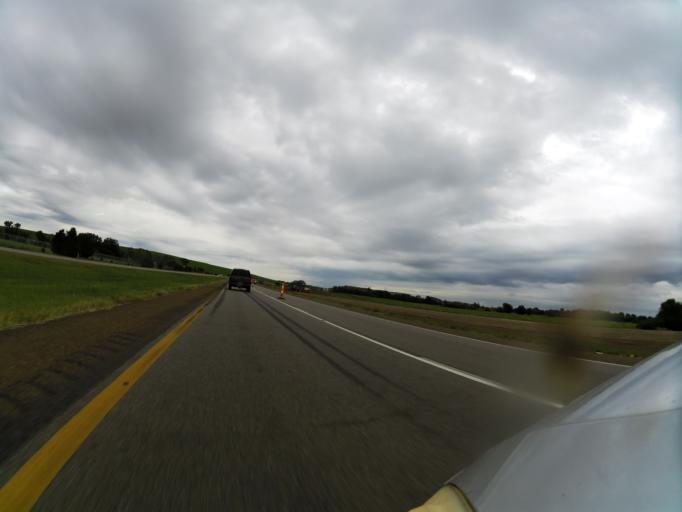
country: US
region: Kansas
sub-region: Sedgwick County
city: Maize
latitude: 37.7597
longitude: -97.4042
